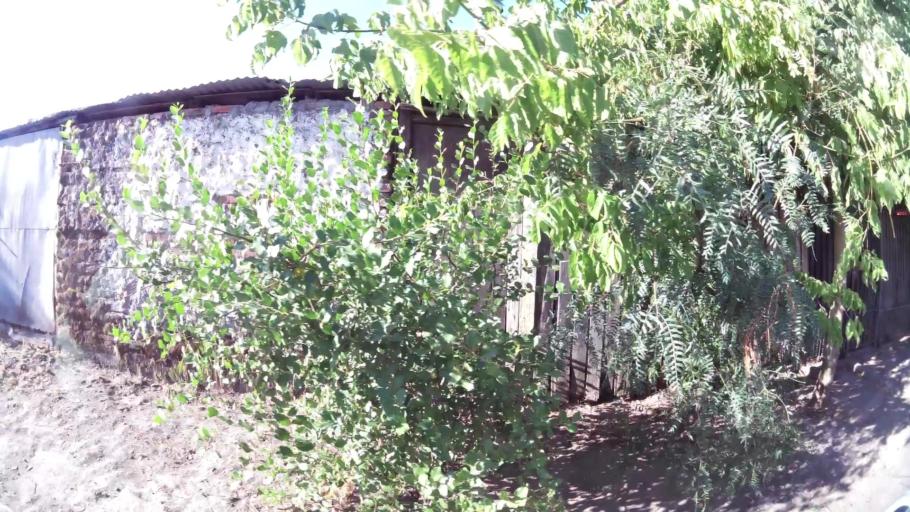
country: CL
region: Maule
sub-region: Provincia de Talca
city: Talca
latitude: -35.4386
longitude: -71.6553
